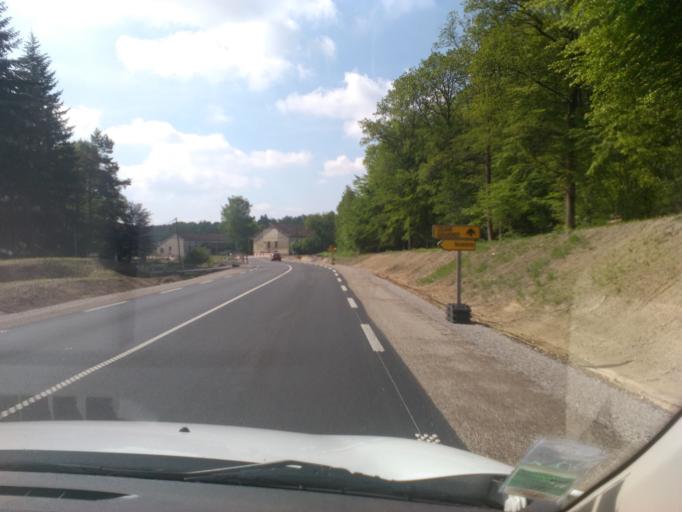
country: FR
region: Lorraine
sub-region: Departement des Vosges
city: Deyvillers
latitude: 48.1805
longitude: 6.4970
